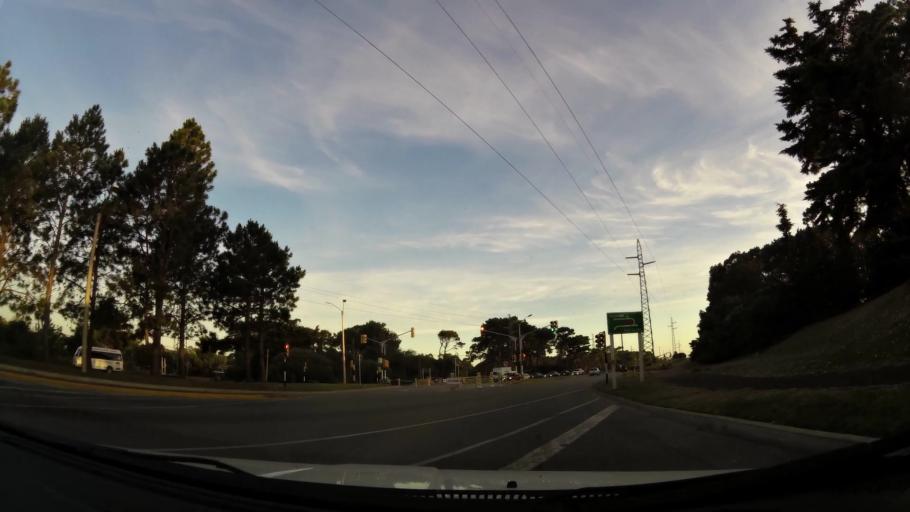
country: UY
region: Maldonado
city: Maldonado
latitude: -34.9253
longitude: -54.9415
